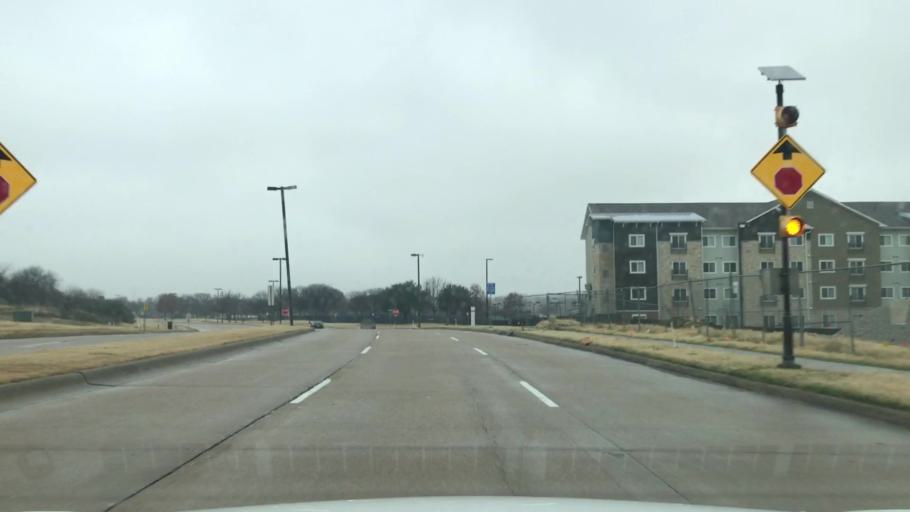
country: US
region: Texas
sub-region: Dallas County
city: Coppell
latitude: 32.9001
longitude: -96.9703
